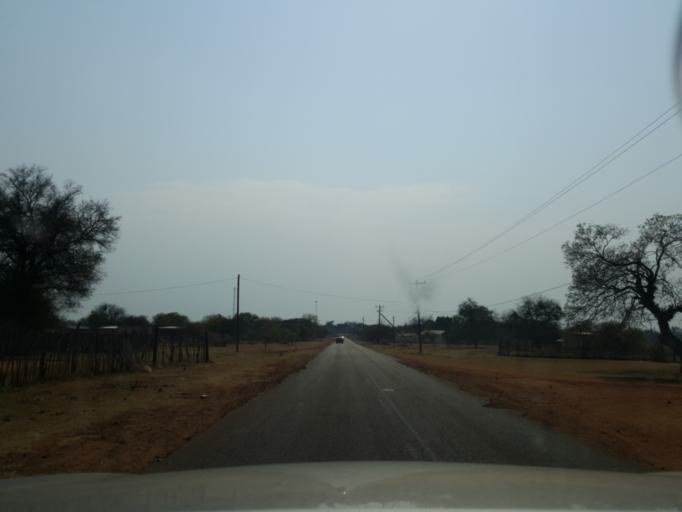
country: BW
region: South East
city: Lobatse
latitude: -25.2885
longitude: 25.9080
